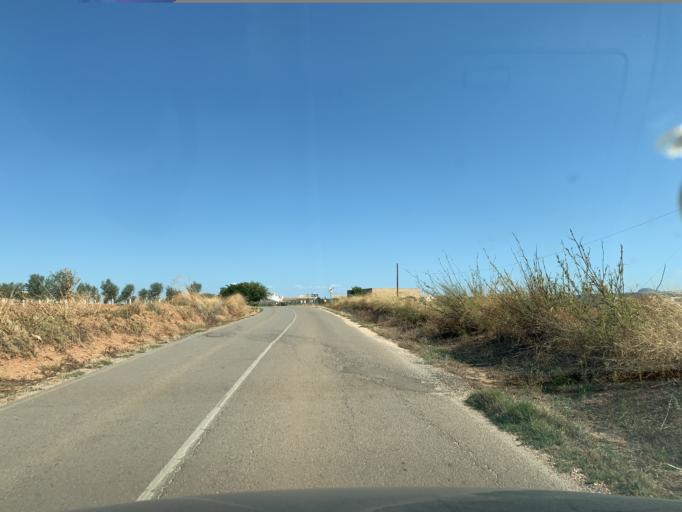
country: ES
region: Andalusia
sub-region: Provincia de Sevilla
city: El Rubio
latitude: 37.3515
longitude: -5.0017
